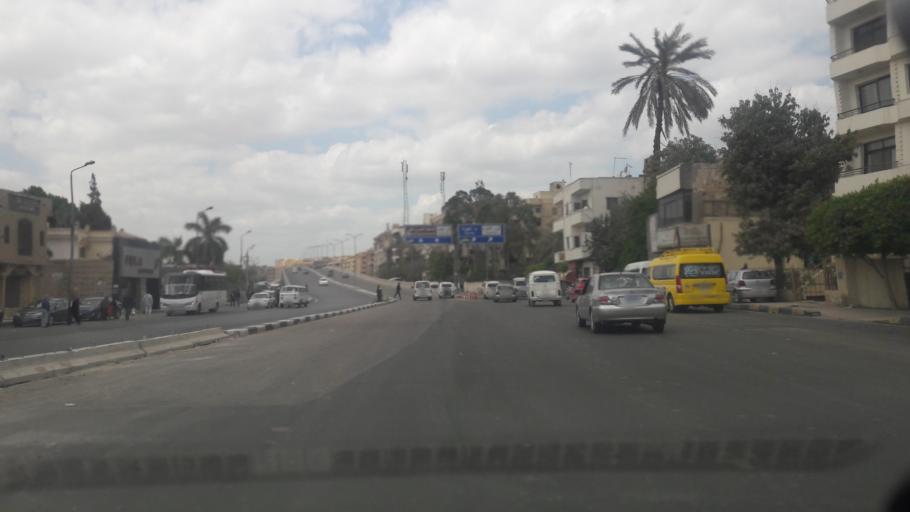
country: EG
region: Al Jizah
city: Al Jizah
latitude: 29.9837
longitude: 31.1428
